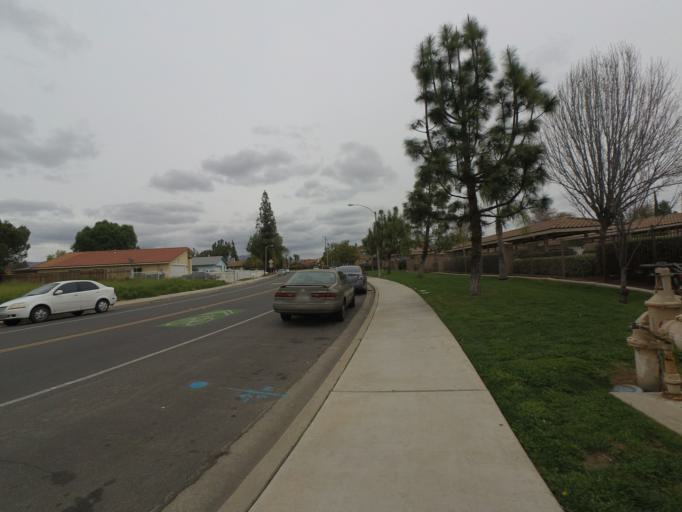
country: US
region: California
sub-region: Riverside County
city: March Air Force Base
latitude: 33.9200
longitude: -117.2631
